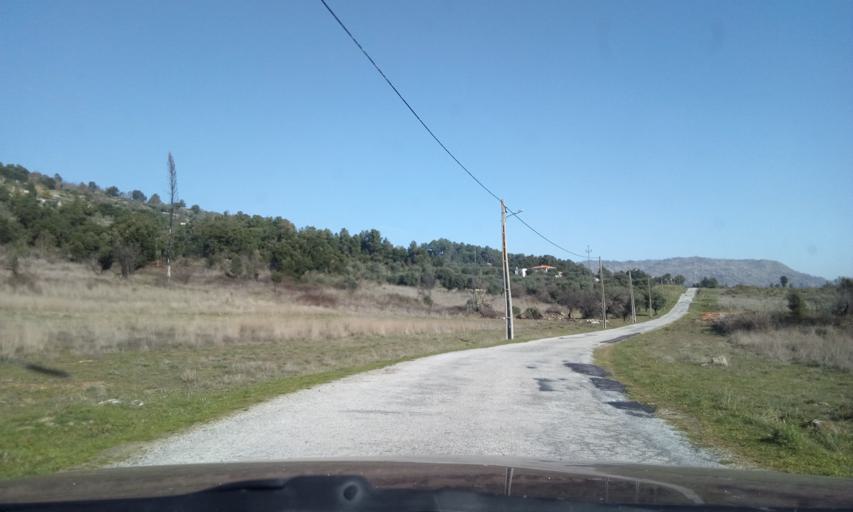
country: PT
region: Guarda
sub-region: Celorico da Beira
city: Celorico da Beira
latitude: 40.6875
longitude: -7.4546
